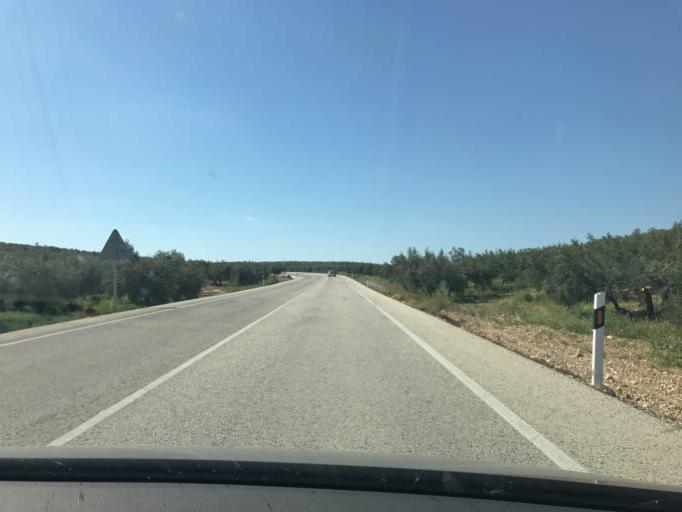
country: ES
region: Andalusia
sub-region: Province of Cordoba
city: Fuente-Tojar
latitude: 37.5618
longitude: -4.1994
